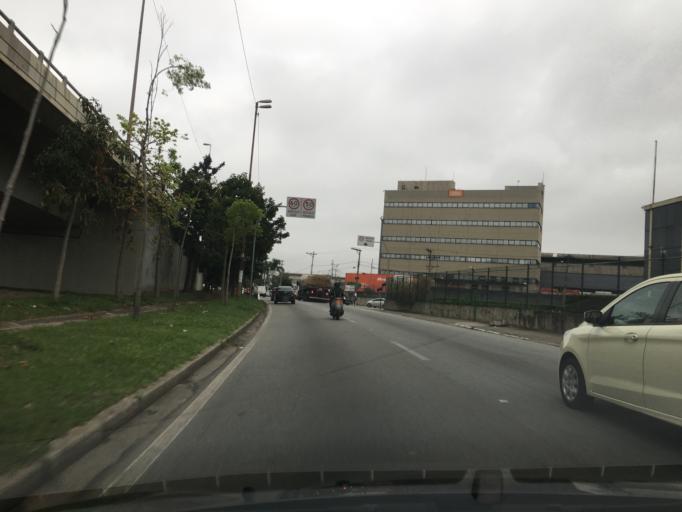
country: BR
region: Sao Paulo
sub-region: Osasco
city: Osasco
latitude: -23.5178
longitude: -46.7458
